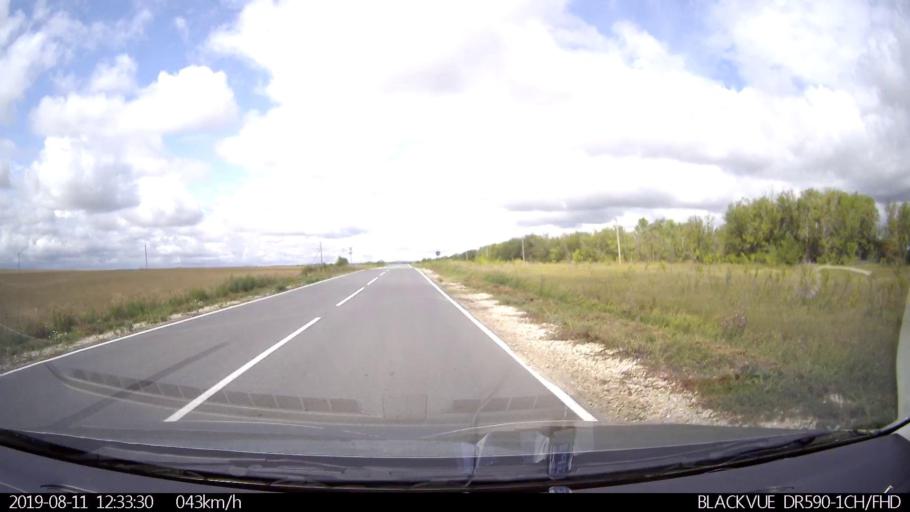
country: RU
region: Ulyanovsk
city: Ignatovka
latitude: 53.8101
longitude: 47.8547
